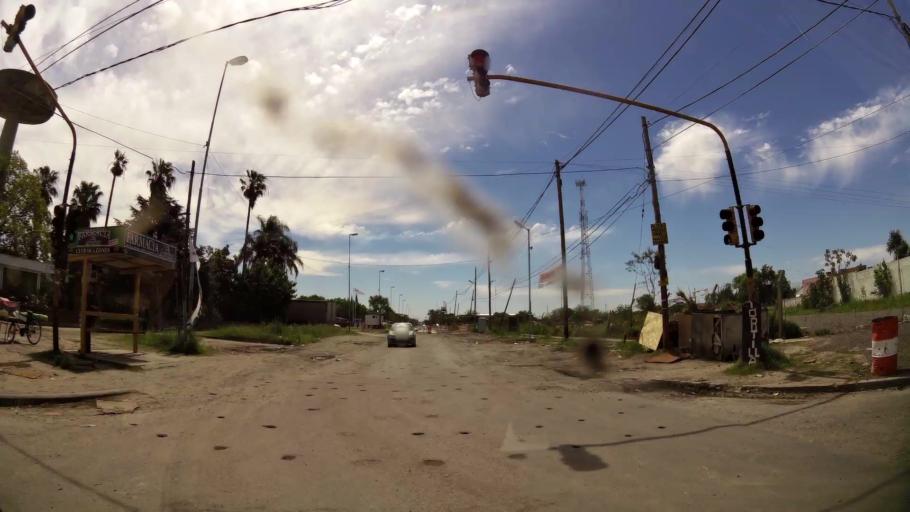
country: AR
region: Buenos Aires
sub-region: Partido de Quilmes
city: Quilmes
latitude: -34.7563
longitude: -58.2986
